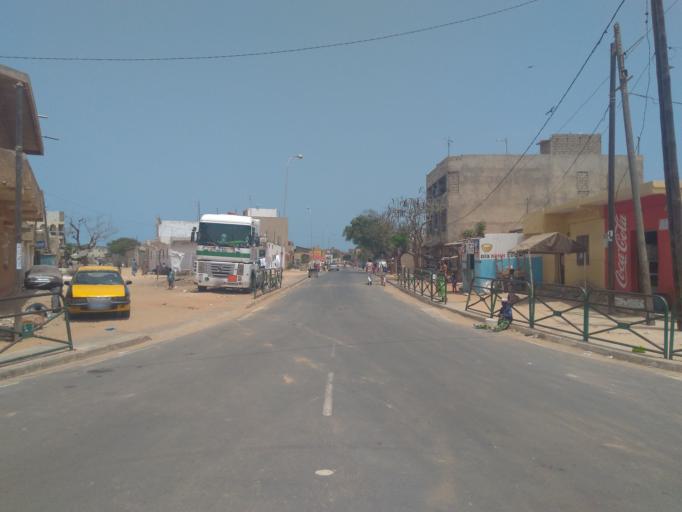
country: SN
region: Dakar
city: Pikine
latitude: 14.7842
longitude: -17.3737
